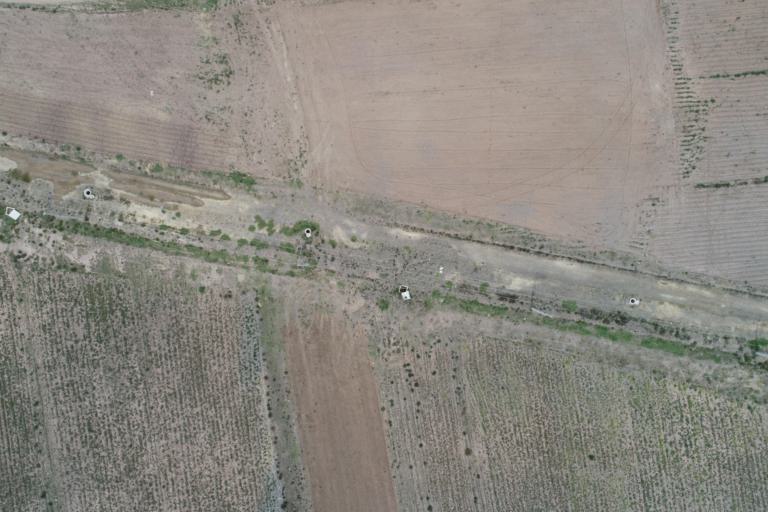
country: BO
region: La Paz
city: La Paz
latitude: -16.5148
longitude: -68.2980
